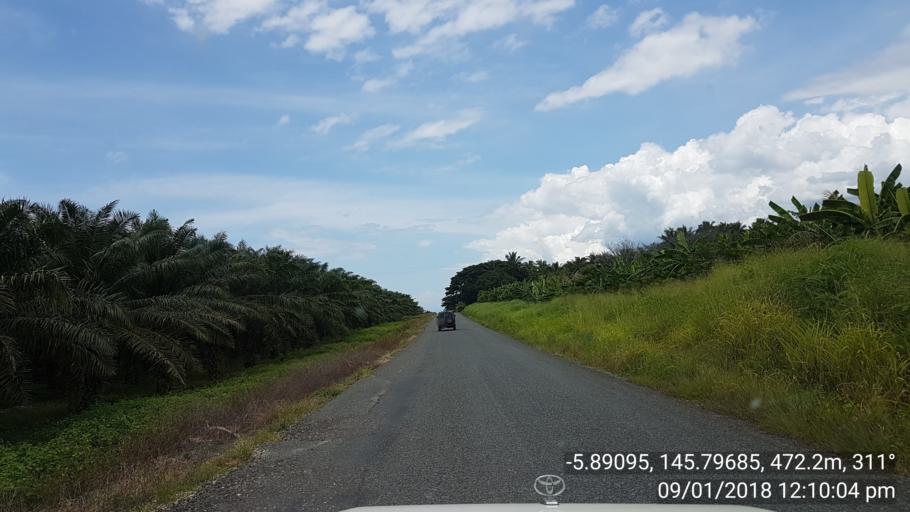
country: PG
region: Eastern Highlands
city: Kainantu
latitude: -5.8911
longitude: 145.7970
